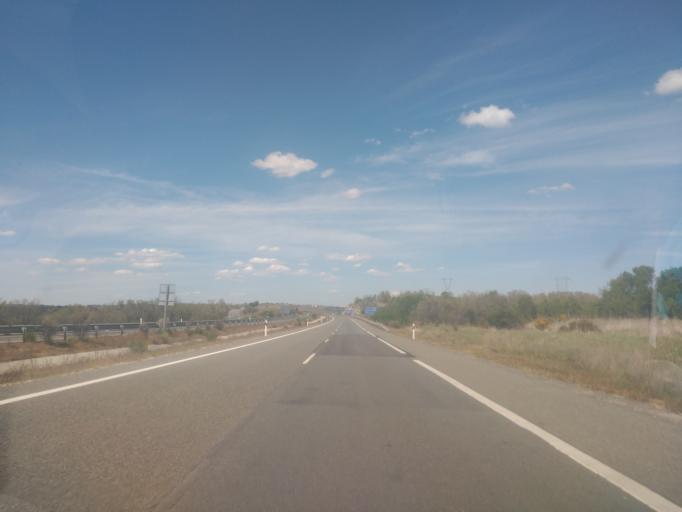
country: ES
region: Castille and Leon
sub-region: Provincia de Salamanca
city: Fuentes de Bejar
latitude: 40.5084
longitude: -5.6748
